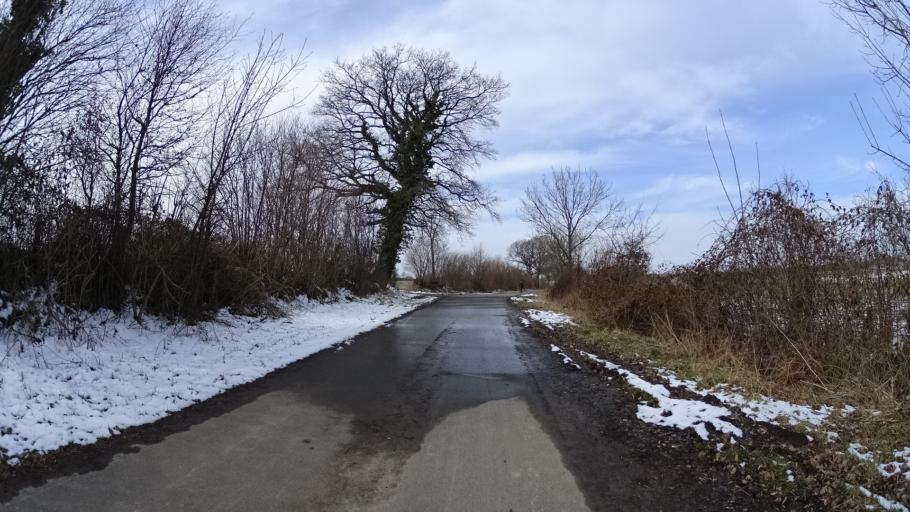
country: DE
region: Schleswig-Holstein
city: Loptin
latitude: 54.1686
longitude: 10.2236
